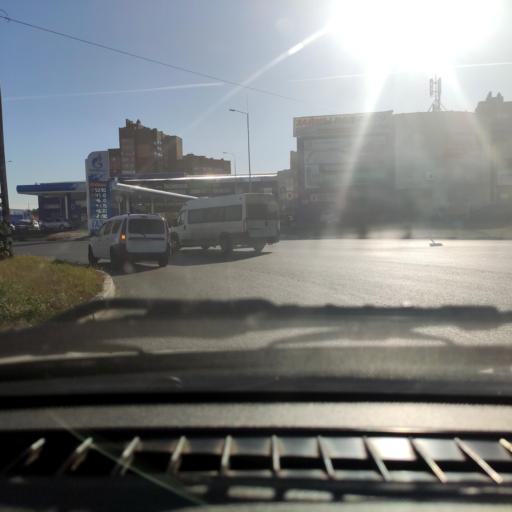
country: RU
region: Samara
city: Tol'yatti
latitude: 53.5396
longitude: 49.3599
